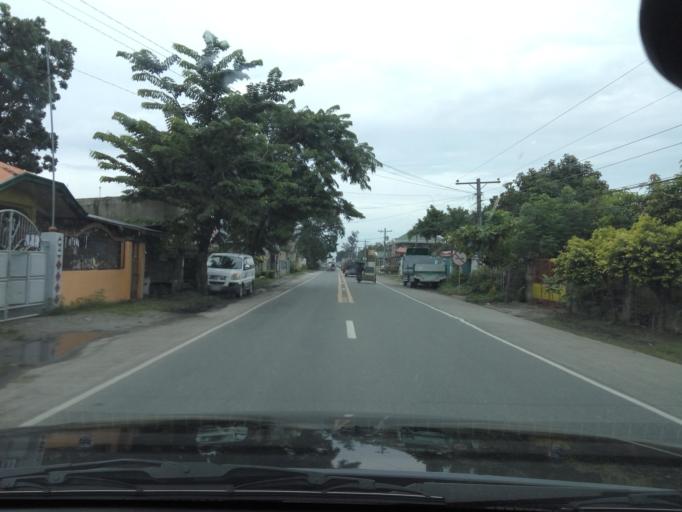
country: PH
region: Central Luzon
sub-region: Province of Nueva Ecija
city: Carmen
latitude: 15.4464
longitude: 120.8240
